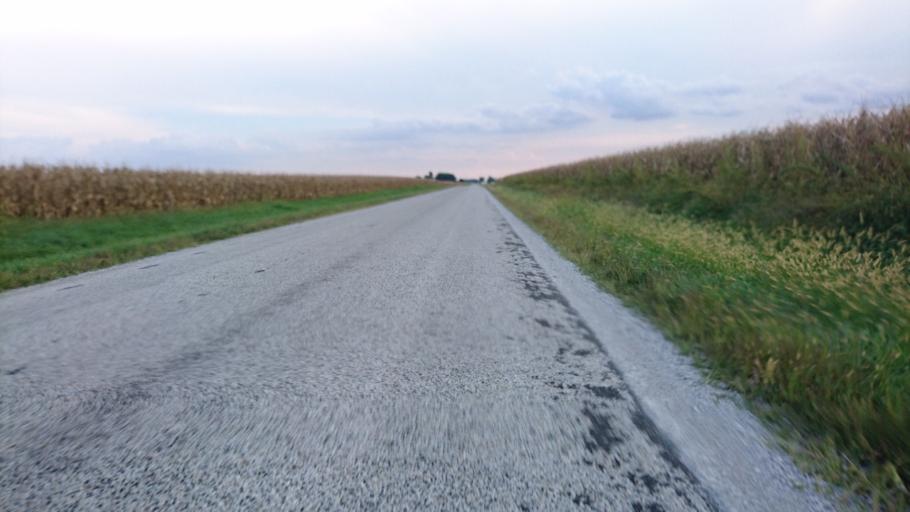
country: US
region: Illinois
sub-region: Logan County
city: Atlanta
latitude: 40.2505
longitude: -89.2051
